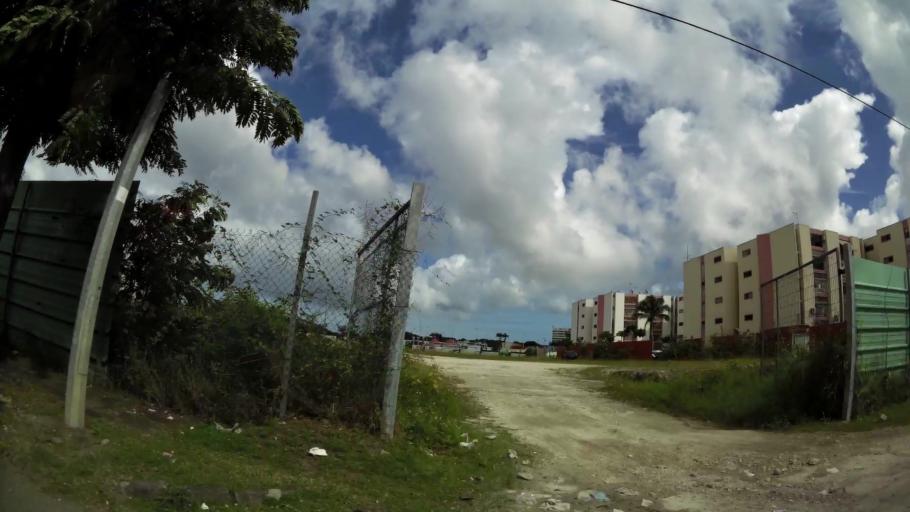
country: GP
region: Guadeloupe
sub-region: Guadeloupe
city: Pointe-a-Pitre
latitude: 16.2492
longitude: -61.5429
